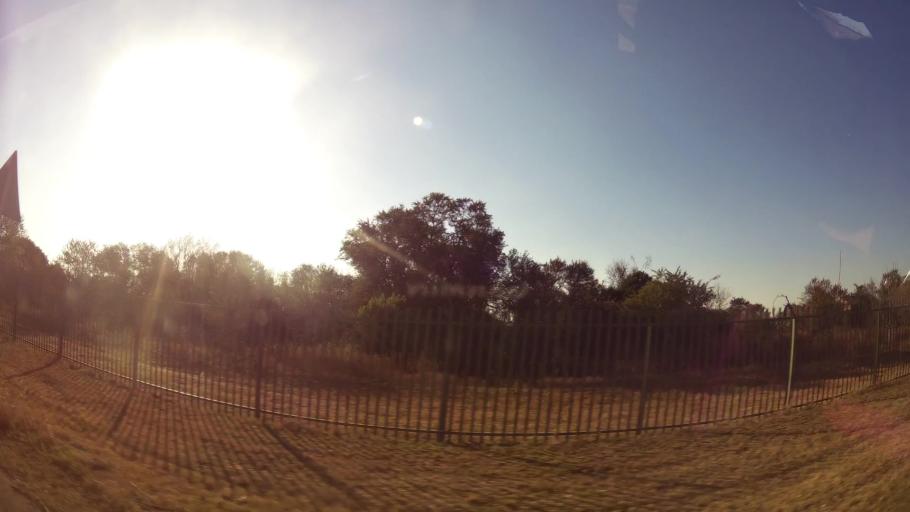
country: ZA
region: Gauteng
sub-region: City of Tshwane Metropolitan Municipality
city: Centurion
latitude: -25.8795
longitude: 28.1487
